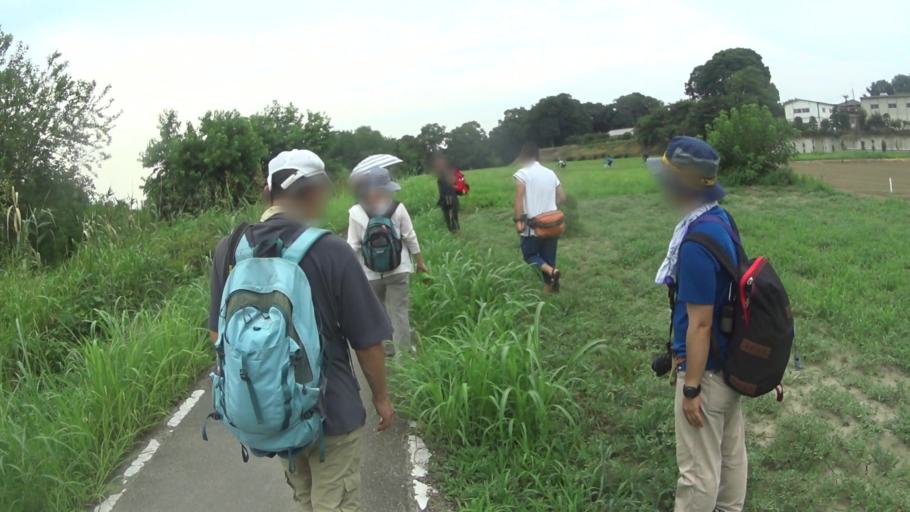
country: JP
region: Saitama
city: Okegawa
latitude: 35.9595
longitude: 139.5413
